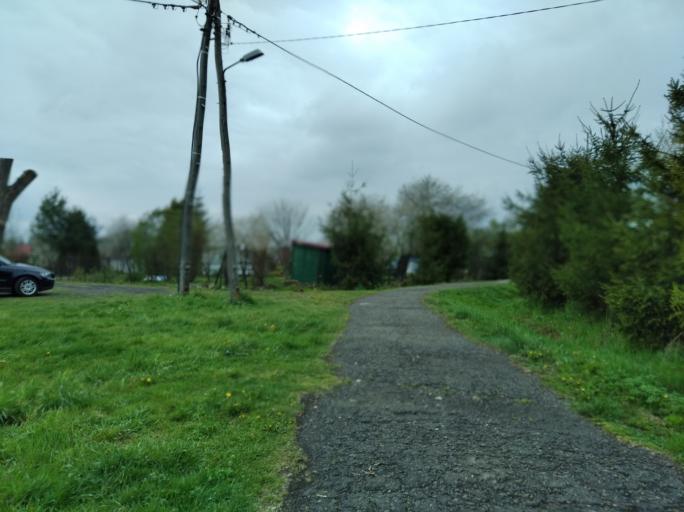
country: PL
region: Subcarpathian Voivodeship
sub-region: Powiat brzozowski
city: Brzozow
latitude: 49.7030
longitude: 22.0168
